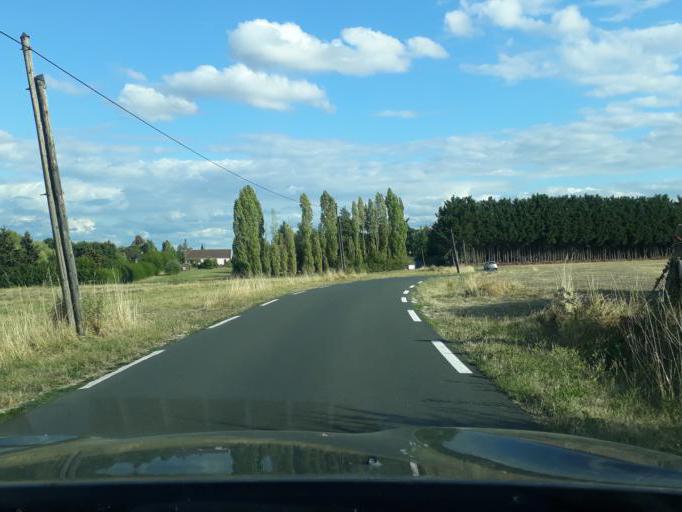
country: FR
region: Centre
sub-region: Departement du Loiret
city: Rebrechien
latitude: 47.9891
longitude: 2.0280
